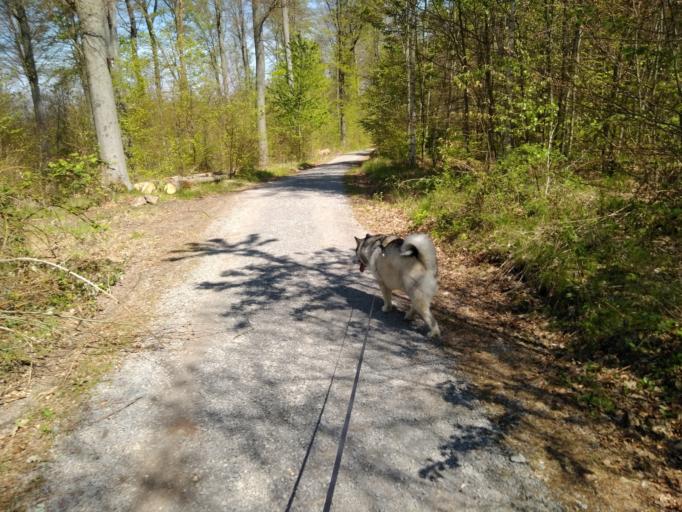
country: DE
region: Baden-Wuerttemberg
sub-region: Regierungsbezirk Stuttgart
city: Gerlingen
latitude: 48.7981
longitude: 9.0895
